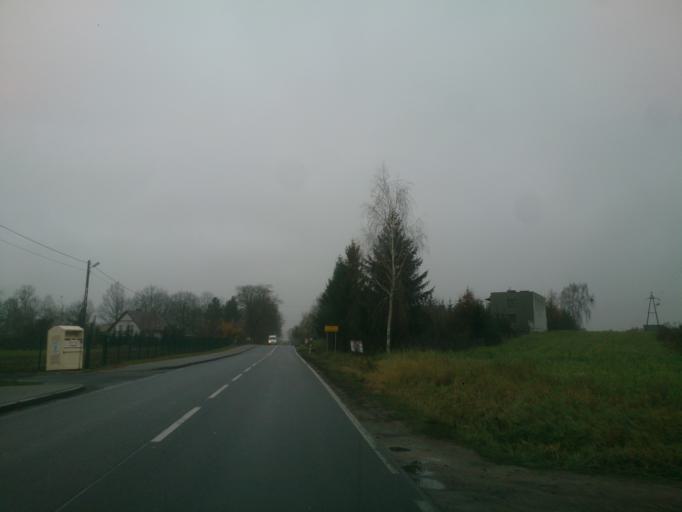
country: PL
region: Kujawsko-Pomorskie
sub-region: Powiat rypinski
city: Rypin
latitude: 53.0560
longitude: 19.4243
